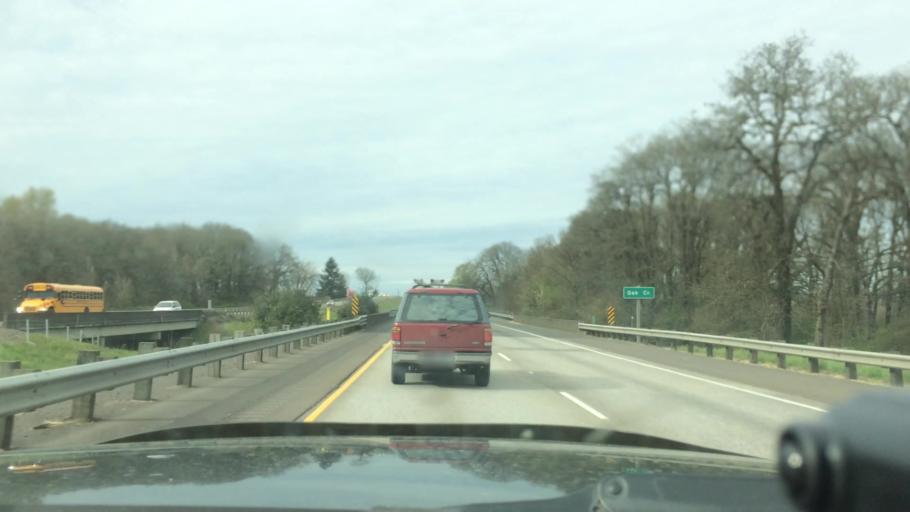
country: US
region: Oregon
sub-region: Linn County
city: Albany
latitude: 44.5897
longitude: -123.0618
